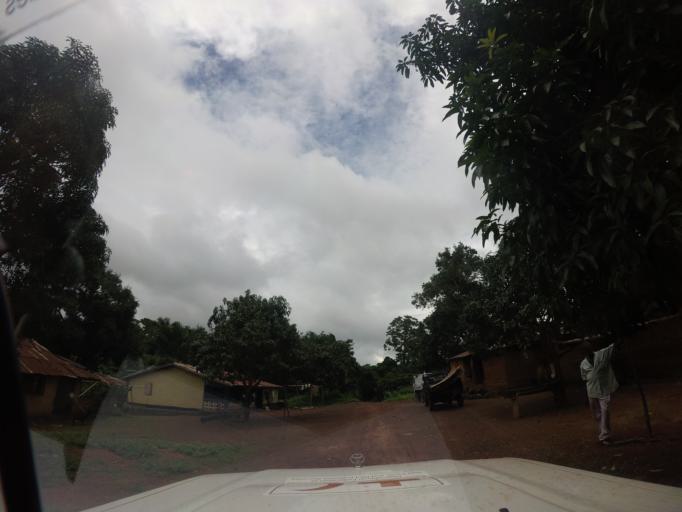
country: SL
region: Northern Province
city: Kamakwie
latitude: 9.6918
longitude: -12.2673
